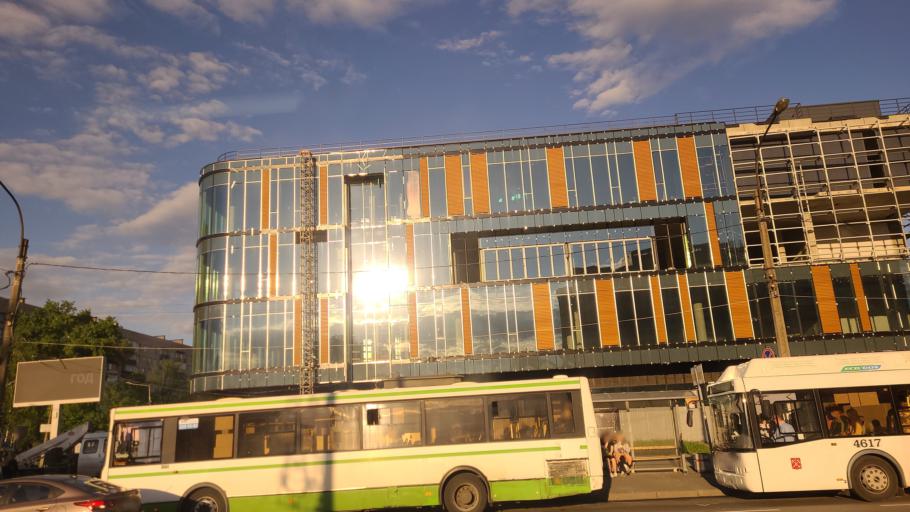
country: RU
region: St.-Petersburg
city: Kolpino
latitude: 59.7411
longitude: 30.5809
